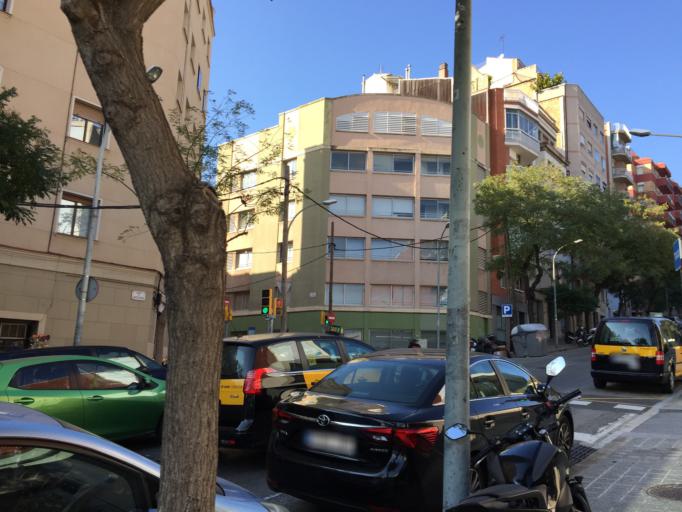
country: ES
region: Catalonia
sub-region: Provincia de Barcelona
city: Horta-Guinardo
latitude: 41.4125
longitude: 2.1727
